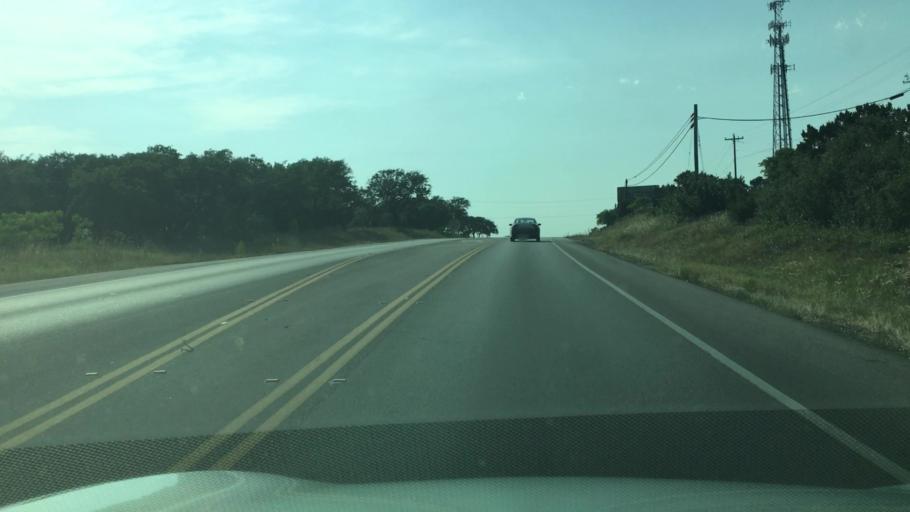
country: US
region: Texas
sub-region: Hays County
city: Wimberley
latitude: 29.9215
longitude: -98.0598
